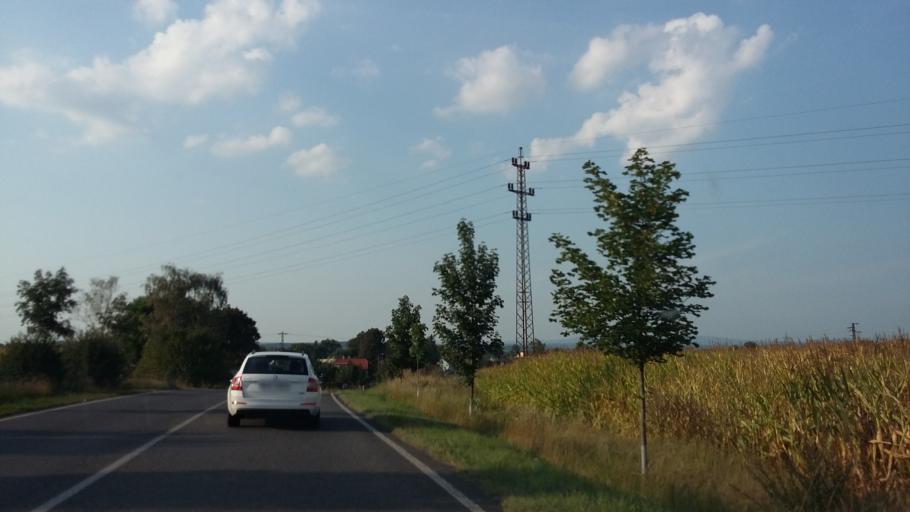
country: CZ
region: Central Bohemia
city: Kosmonosy
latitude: 50.4532
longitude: 14.9309
